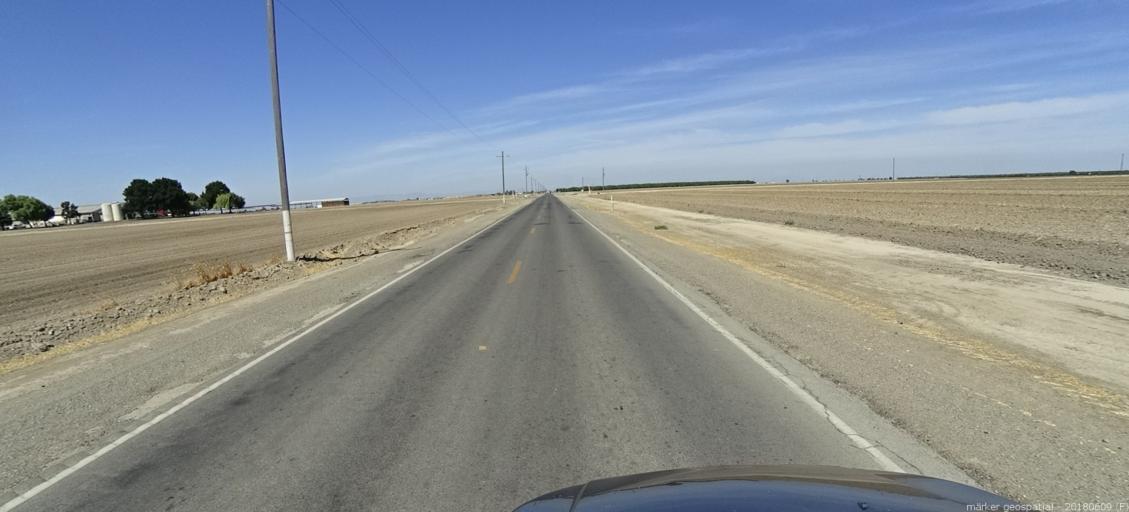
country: US
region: California
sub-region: Madera County
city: Fairmead
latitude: 36.9528
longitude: -120.2447
